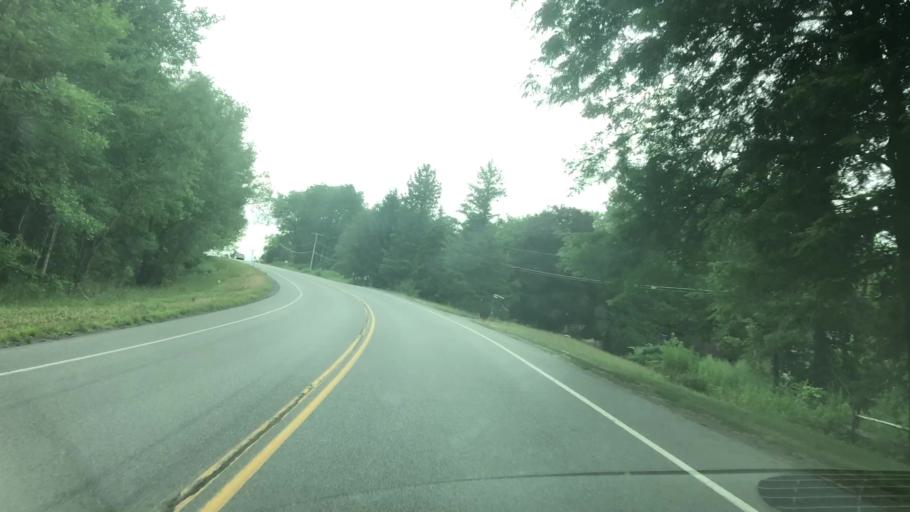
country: US
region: New York
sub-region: Wayne County
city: Macedon
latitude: 43.1348
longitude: -77.3552
